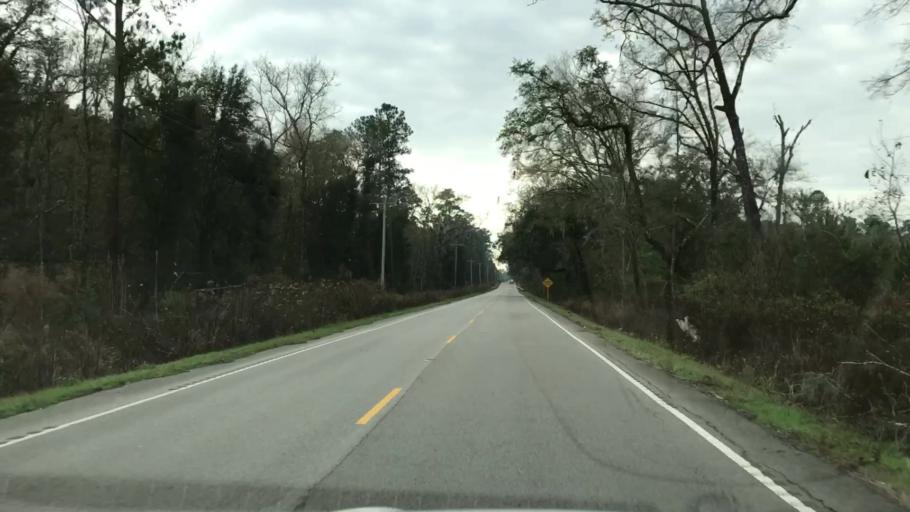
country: US
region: South Carolina
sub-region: Jasper County
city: Ridgeland
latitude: 32.5109
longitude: -80.8884
